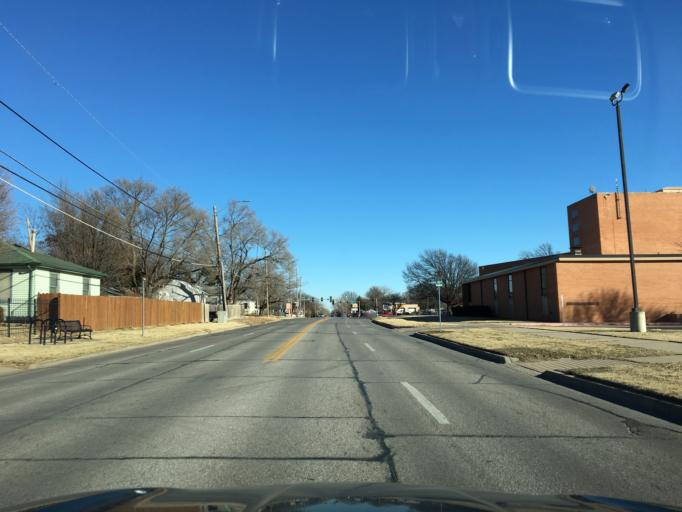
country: US
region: Kansas
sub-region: Sedgwick County
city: Wichita
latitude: 37.6719
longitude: -97.2739
